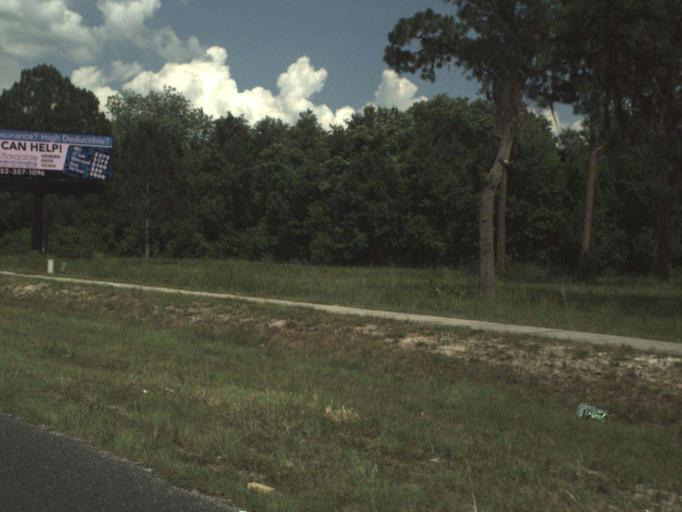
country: US
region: Florida
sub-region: Lake County
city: Silver Lake
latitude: 28.8295
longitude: -81.8239
